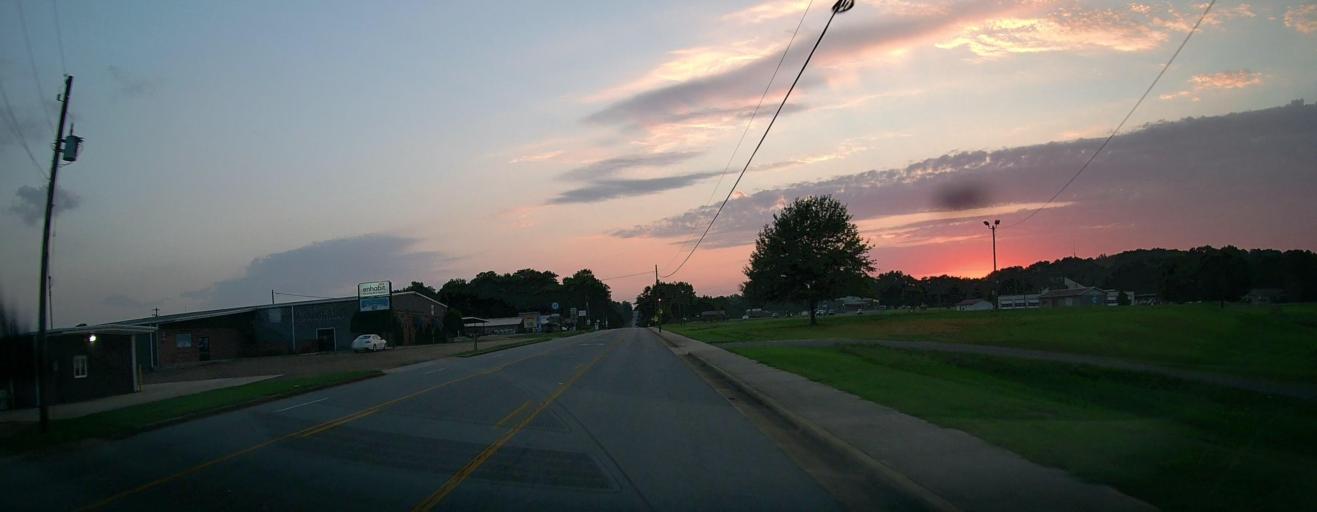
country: US
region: Alabama
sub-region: Marion County
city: Hamilton
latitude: 34.1377
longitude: -87.9927
